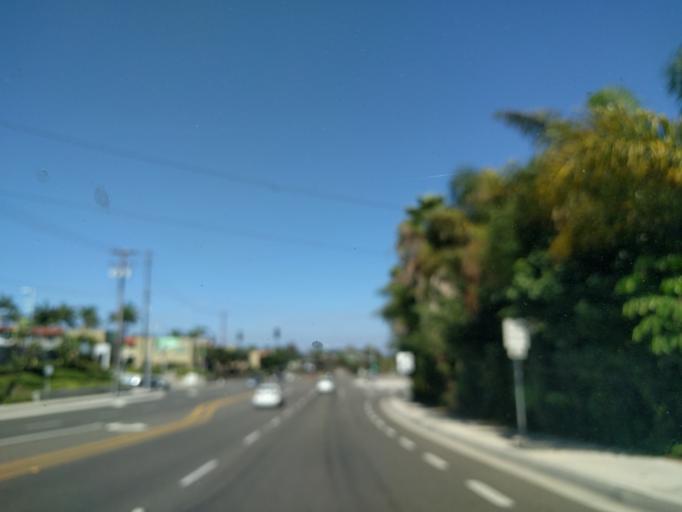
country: US
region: California
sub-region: Orange County
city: Costa Mesa
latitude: 33.6579
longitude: -117.8850
